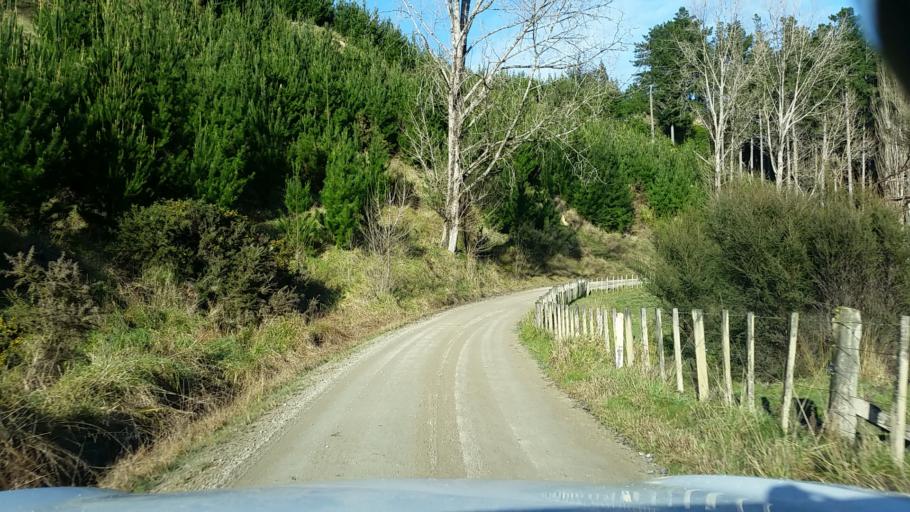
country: NZ
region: Taranaki
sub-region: South Taranaki District
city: Patea
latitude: -39.6993
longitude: 174.7391
